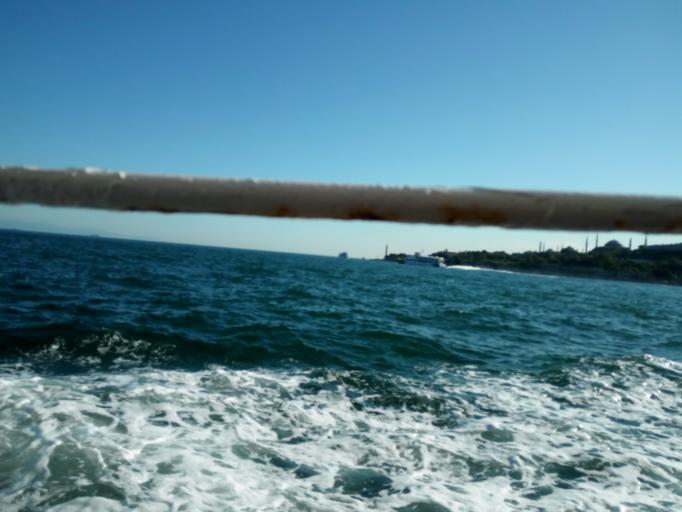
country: TR
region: Istanbul
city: Eminoenue
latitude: 41.0152
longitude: 28.9942
